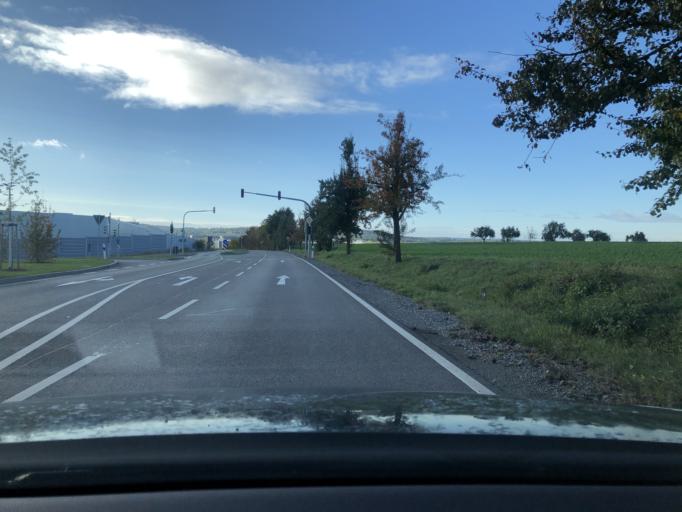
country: DE
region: Baden-Wuerttemberg
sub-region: Regierungsbezirk Stuttgart
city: Magstadt
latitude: 48.7016
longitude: 8.9770
